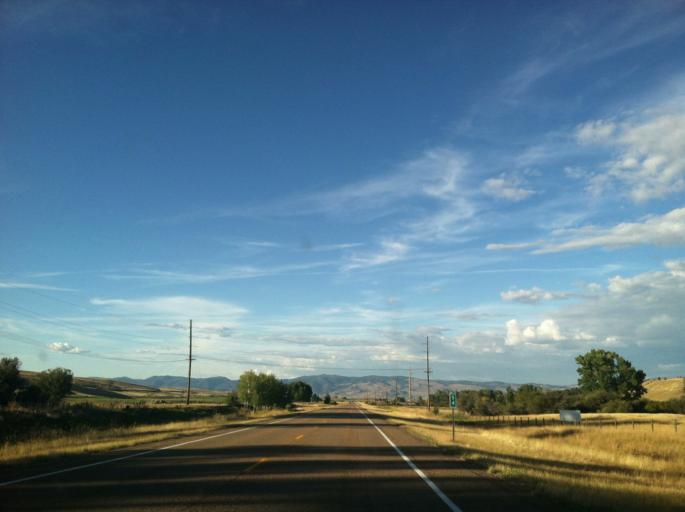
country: US
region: Montana
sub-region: Granite County
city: Philipsburg
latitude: 46.5395
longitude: -113.2211
